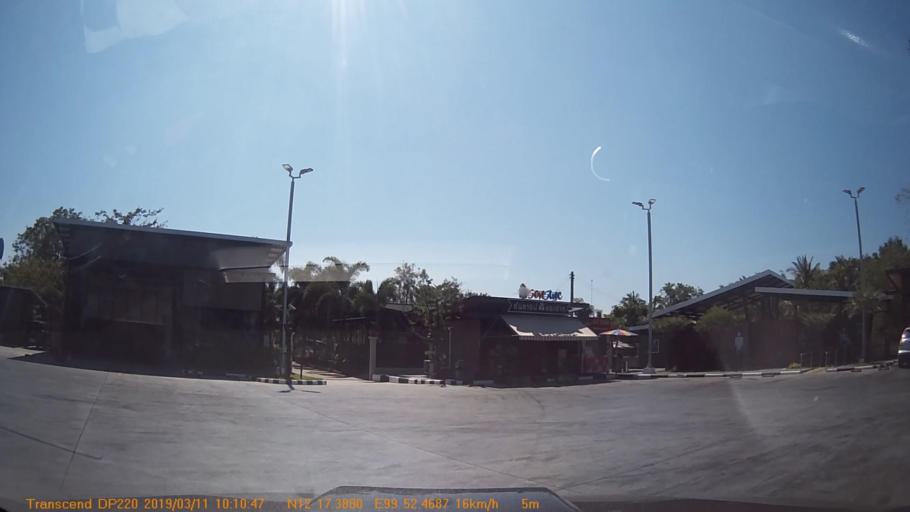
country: TH
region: Prachuap Khiri Khan
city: Sam Roi Yot
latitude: 12.2897
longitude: 99.8745
